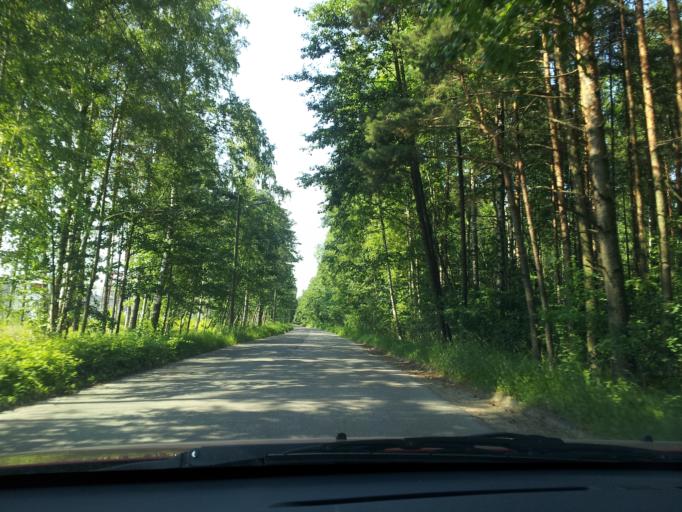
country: LV
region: Riga
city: Bolderaja
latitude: 57.0579
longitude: 24.0589
